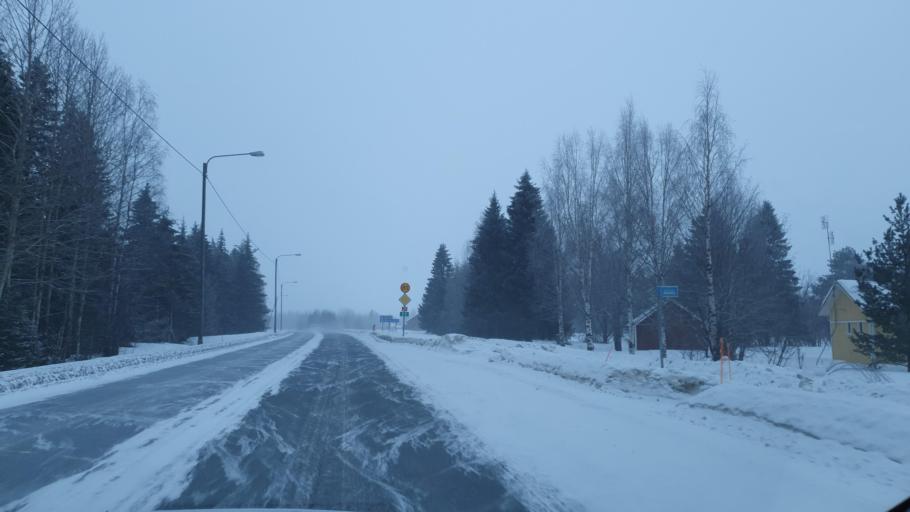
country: FI
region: Lapland
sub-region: Kemi-Tornio
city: Tornio
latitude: 65.9431
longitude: 24.0835
